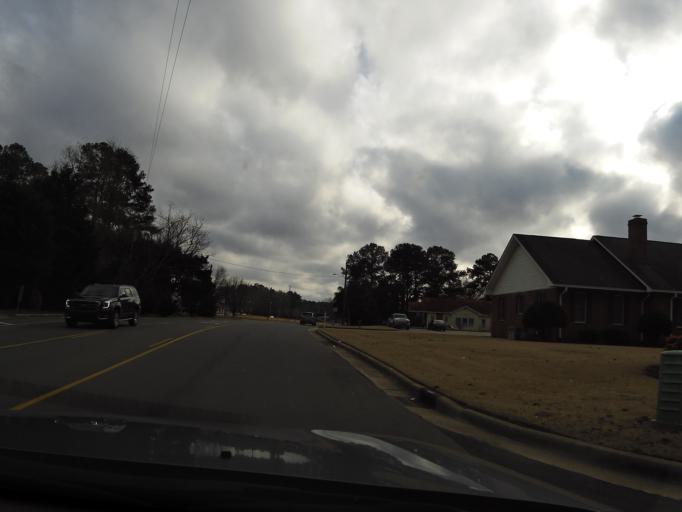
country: US
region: North Carolina
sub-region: Nash County
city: Rocky Mount
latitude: 35.9530
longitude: -77.8484
